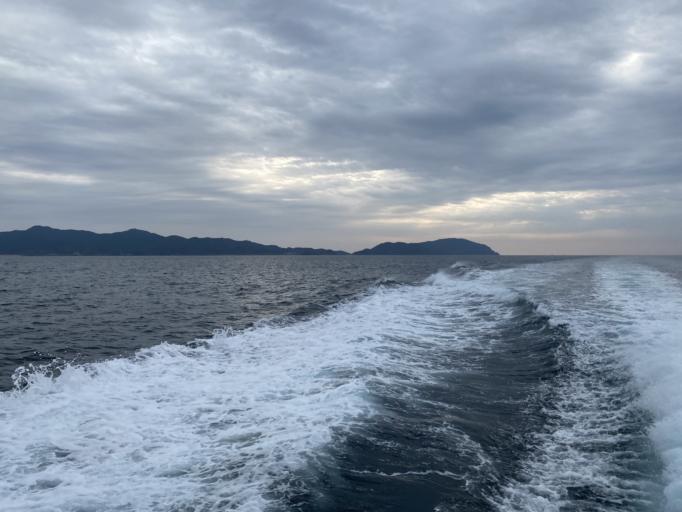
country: JP
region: Nagasaki
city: Nagasaki-shi
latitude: 32.6371
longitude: 129.7597
